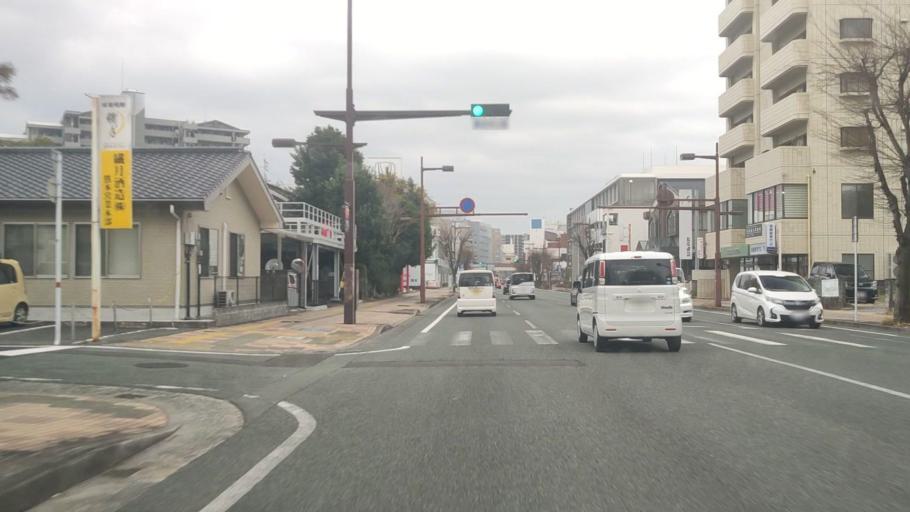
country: JP
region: Kumamoto
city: Kumamoto
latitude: 32.8027
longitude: 130.7200
